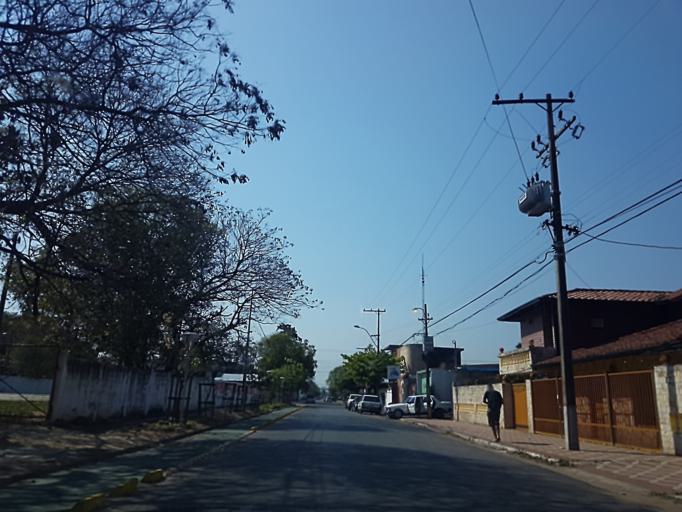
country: PY
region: Central
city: Colonia Mariano Roque Alonso
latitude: -25.2132
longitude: -57.5328
